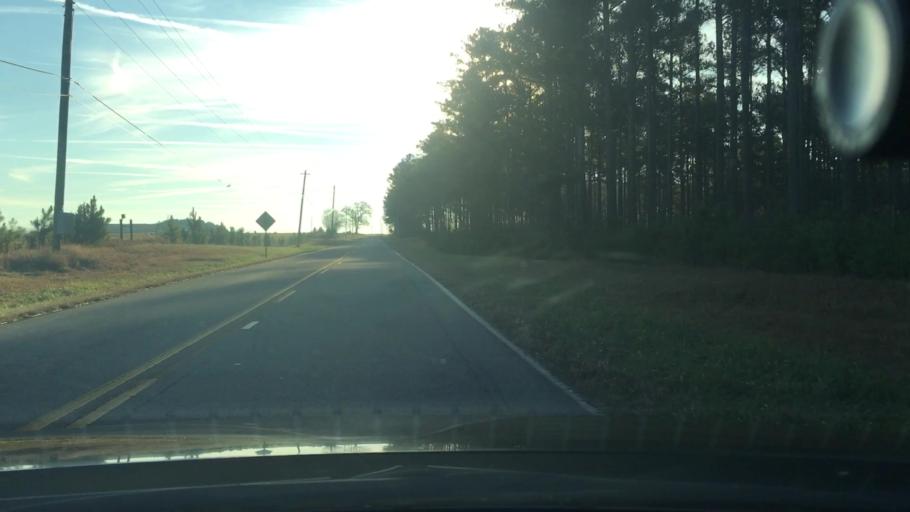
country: US
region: Georgia
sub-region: Spalding County
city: Experiment
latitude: 33.2664
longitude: -84.3114
